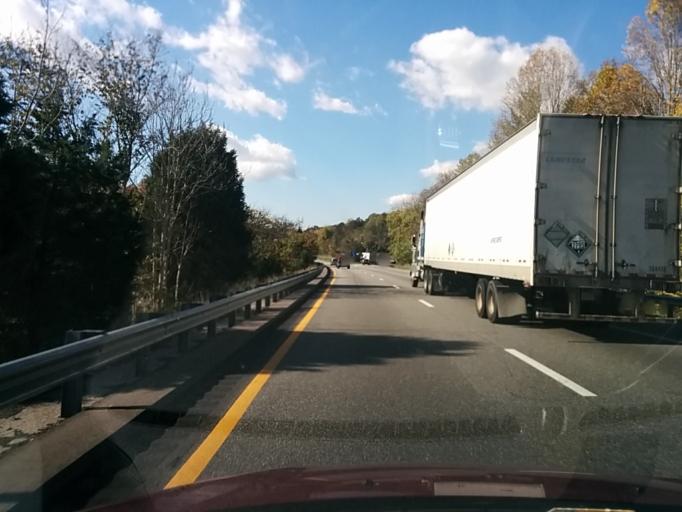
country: US
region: Virginia
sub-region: Botetourt County
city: Fincastle
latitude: 37.4704
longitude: -79.8086
